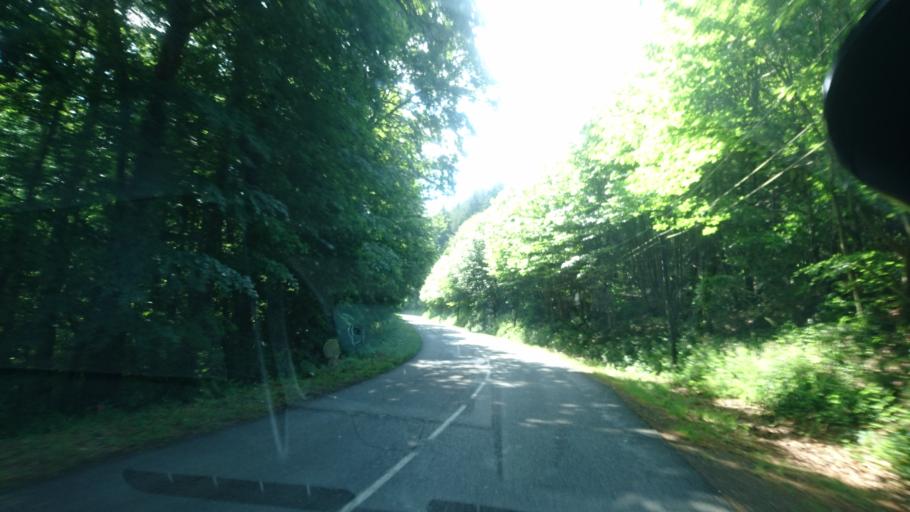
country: FR
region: Limousin
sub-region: Departement de la Haute-Vienne
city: Peyrat-le-Chateau
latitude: 45.8126
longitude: 1.8087
